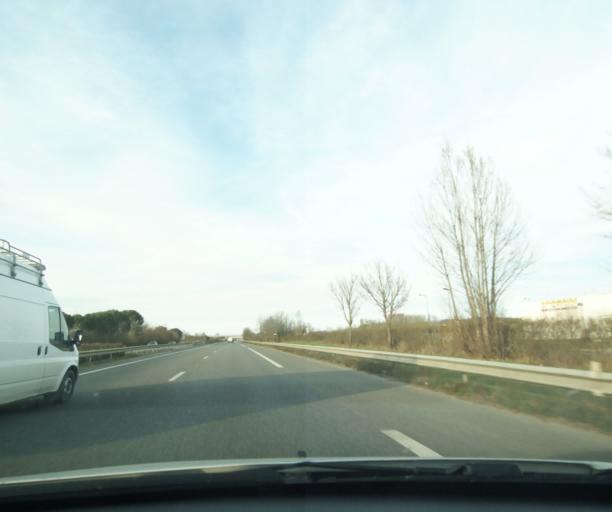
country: FR
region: Midi-Pyrenees
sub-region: Departement de la Haute-Garonne
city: Le Fauga
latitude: 43.3946
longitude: 1.2875
